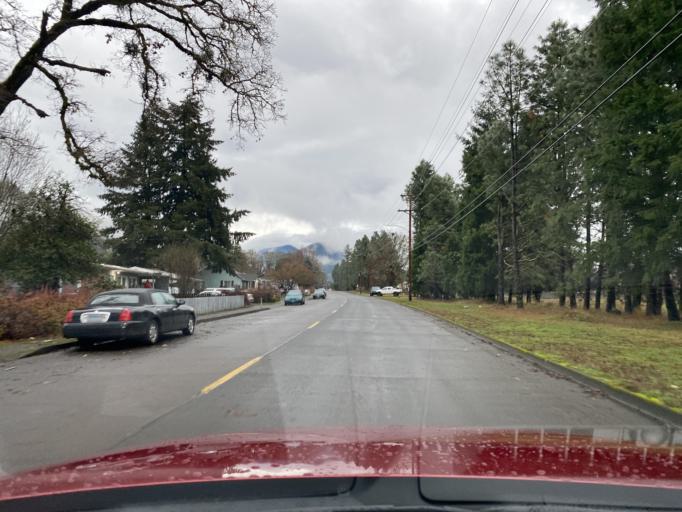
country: US
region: Oregon
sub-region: Lane County
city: Oakridge
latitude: 43.7475
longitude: -122.4770
